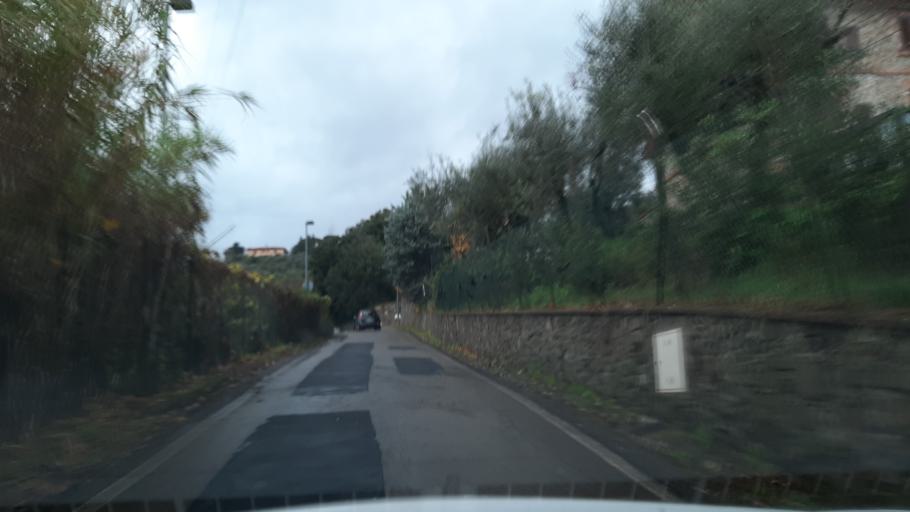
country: IT
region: Tuscany
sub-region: Province of Florence
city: Fiesole
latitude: 43.8068
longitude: 11.2684
